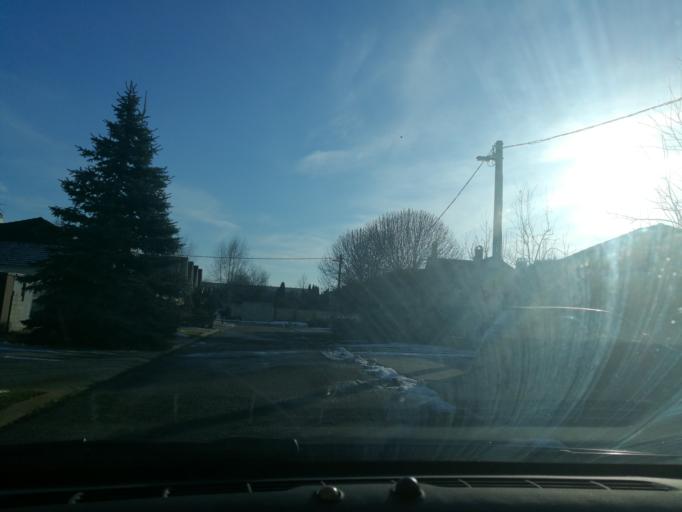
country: HU
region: Szabolcs-Szatmar-Bereg
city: Nyiregyhaza
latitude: 47.9644
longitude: 21.7397
